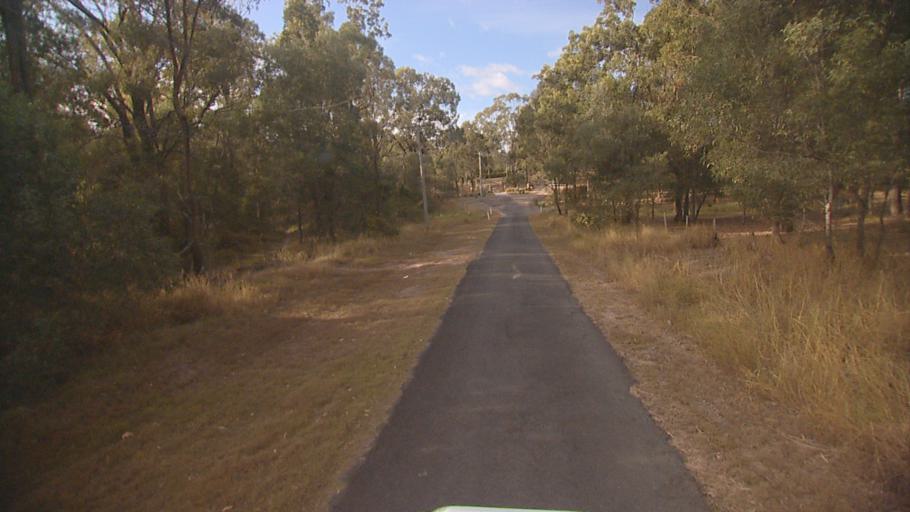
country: AU
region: Queensland
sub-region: Logan
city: Cedar Vale
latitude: -27.8722
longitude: 153.0242
